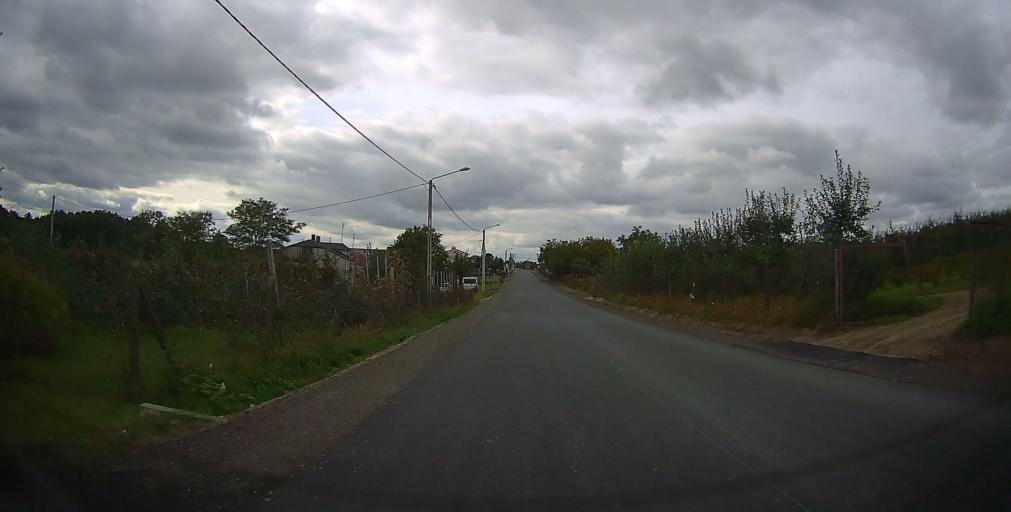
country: PL
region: Masovian Voivodeship
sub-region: Powiat grojecki
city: Belsk Duzy
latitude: 51.8082
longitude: 20.8452
